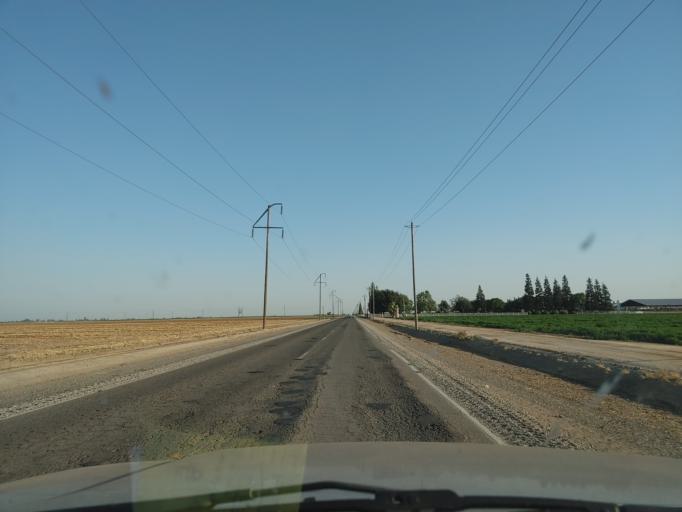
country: US
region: California
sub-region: Madera County
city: Chowchilla
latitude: 37.1623
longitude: -120.3831
